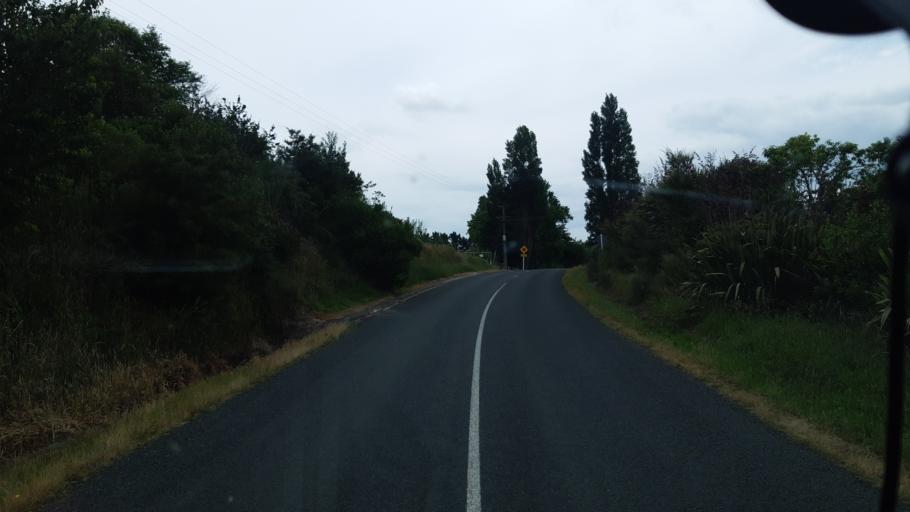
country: NZ
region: Waikato
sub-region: Waikato District
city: Raglan
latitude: -37.8476
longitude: 175.0331
